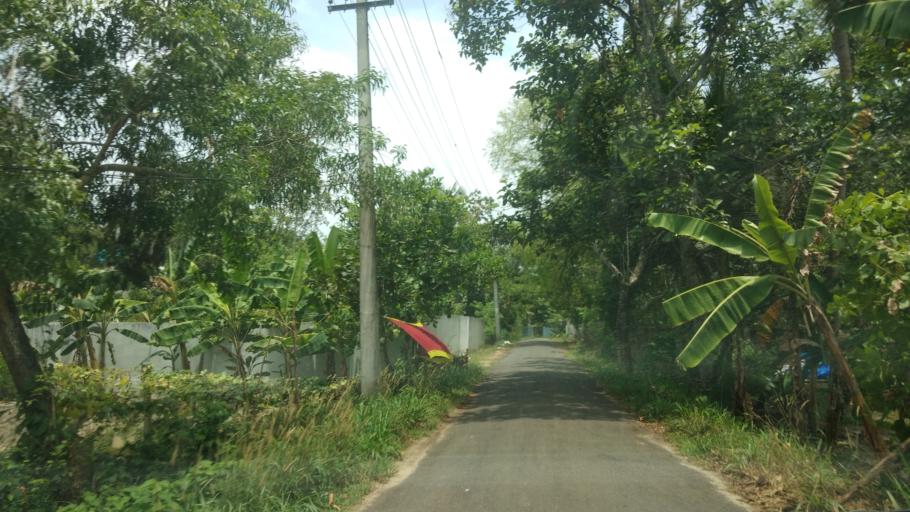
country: IN
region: Kerala
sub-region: Alappuzha
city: Shertallai
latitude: 9.6502
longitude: 76.3333
